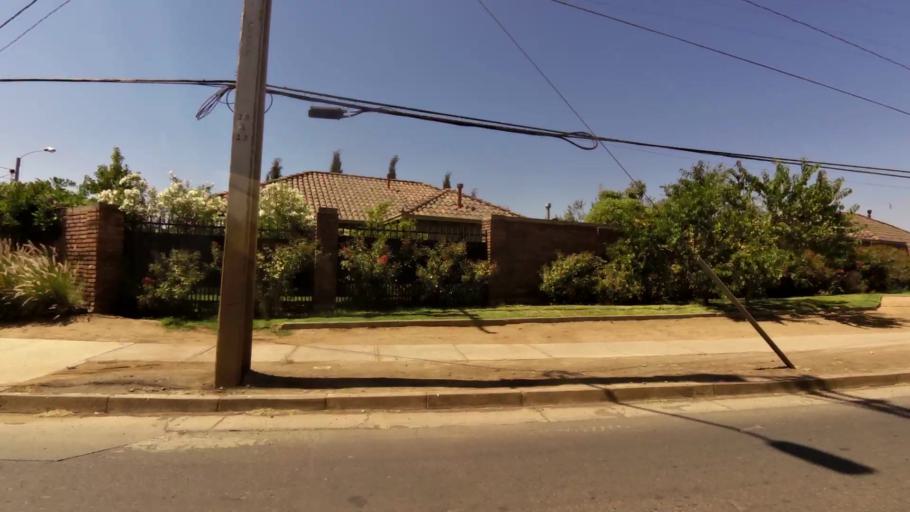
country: CL
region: Maule
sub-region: Provincia de Talca
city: Talca
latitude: -35.4325
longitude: -71.5999
